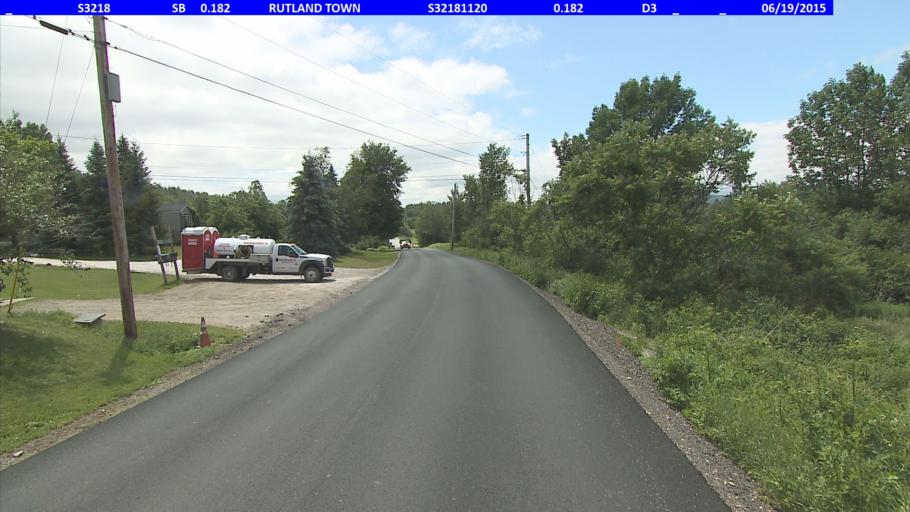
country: US
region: Vermont
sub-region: Rutland County
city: Rutland
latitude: 43.5886
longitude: -72.9512
